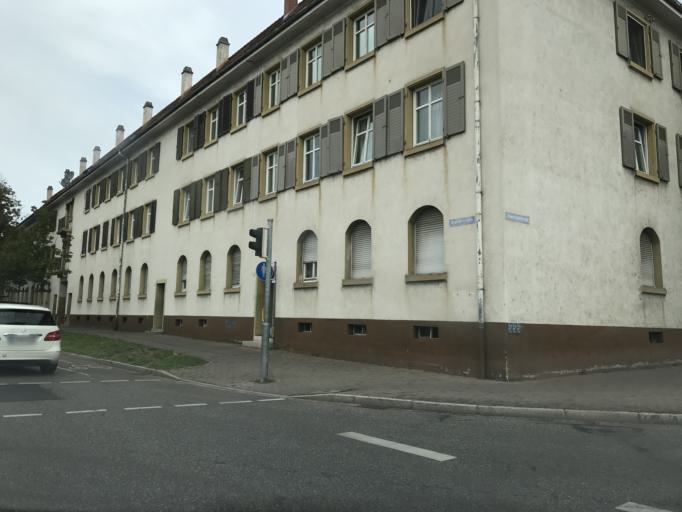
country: DE
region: Baden-Wuerttemberg
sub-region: Freiburg Region
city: Loerrach
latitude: 47.6177
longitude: 7.6666
